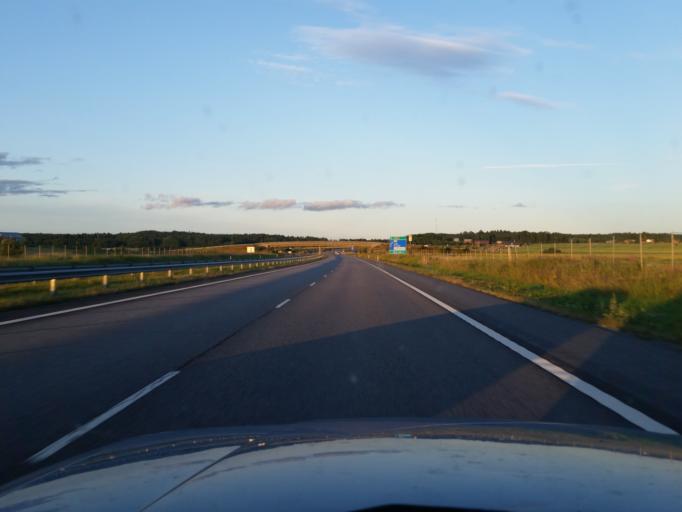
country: FI
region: Varsinais-Suomi
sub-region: Salo
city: Halikko
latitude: 60.4284
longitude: 23.0219
